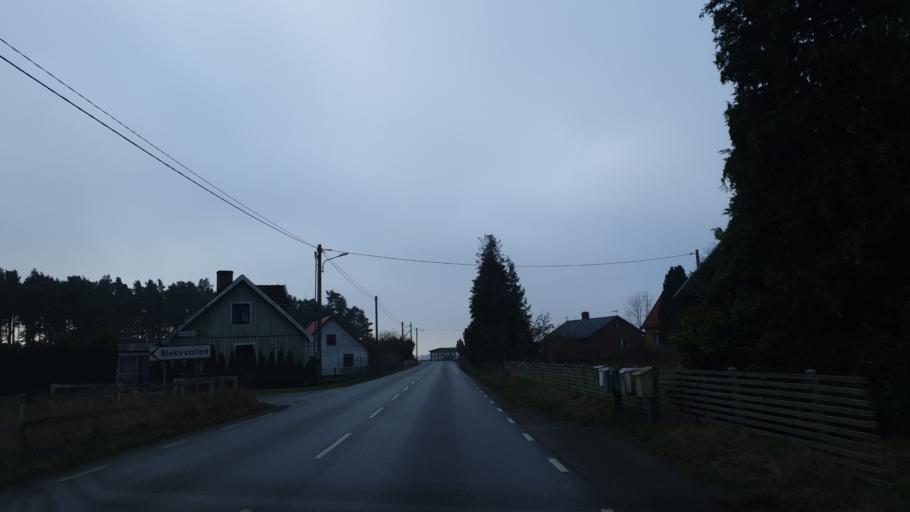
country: SE
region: Skane
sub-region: Kristianstads Kommun
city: Fjalkinge
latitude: 55.9976
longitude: 14.3513
